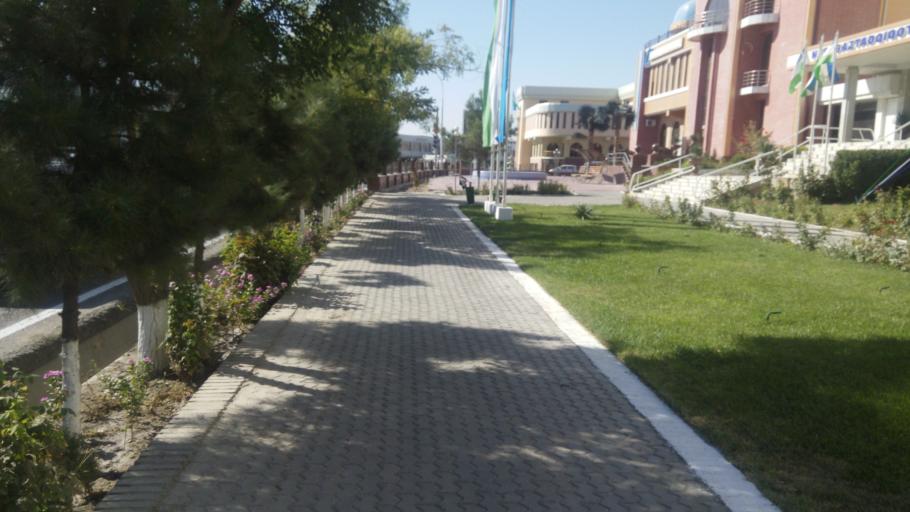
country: UZ
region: Bukhara
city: Bukhara
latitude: 39.7743
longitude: 64.4314
